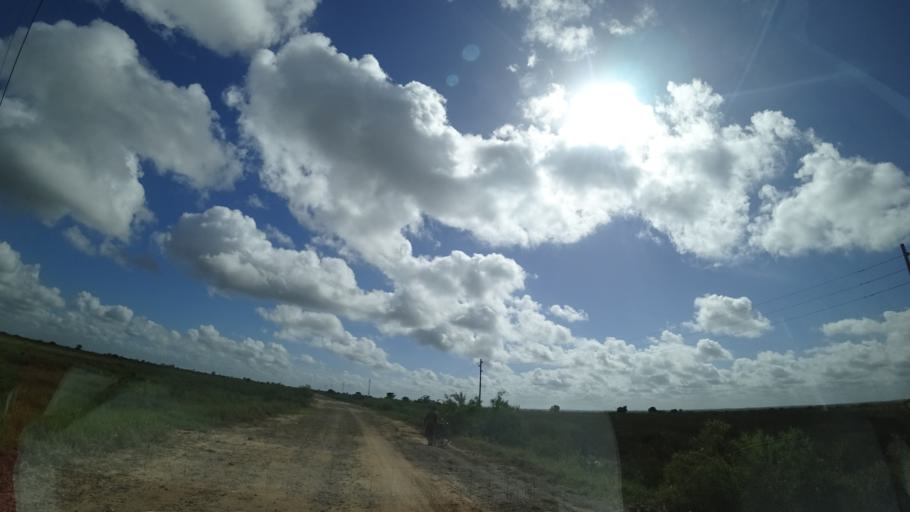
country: MZ
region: Sofala
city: Dondo
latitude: -19.4594
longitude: 34.5631
